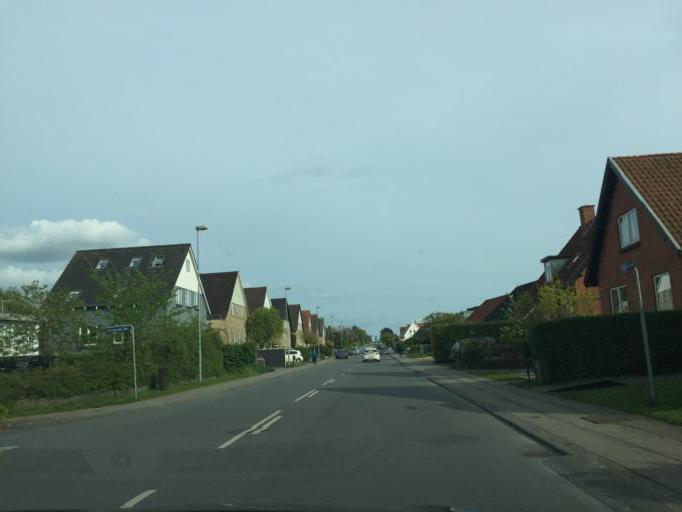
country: DK
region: South Denmark
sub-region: Odense Kommune
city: Odense
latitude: 55.3671
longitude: 10.3574
